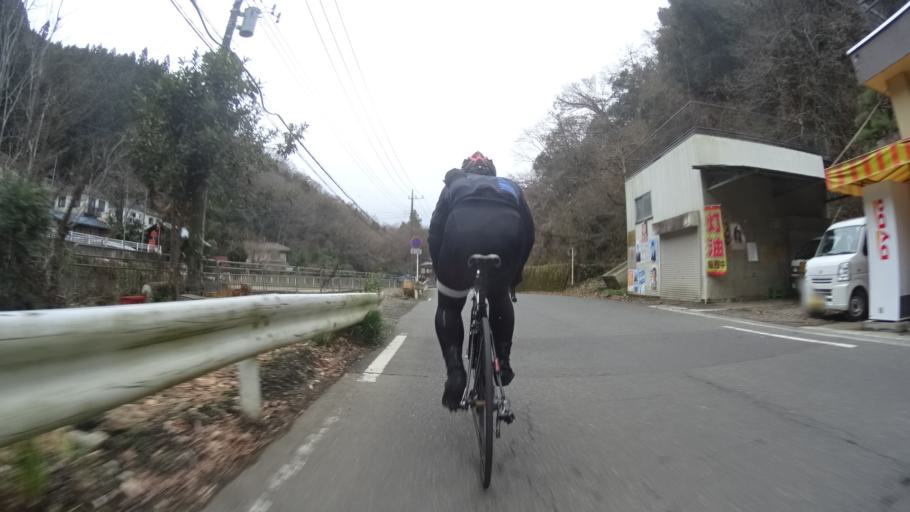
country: JP
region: Yamanashi
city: Uenohara
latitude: 35.6253
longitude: 139.1505
